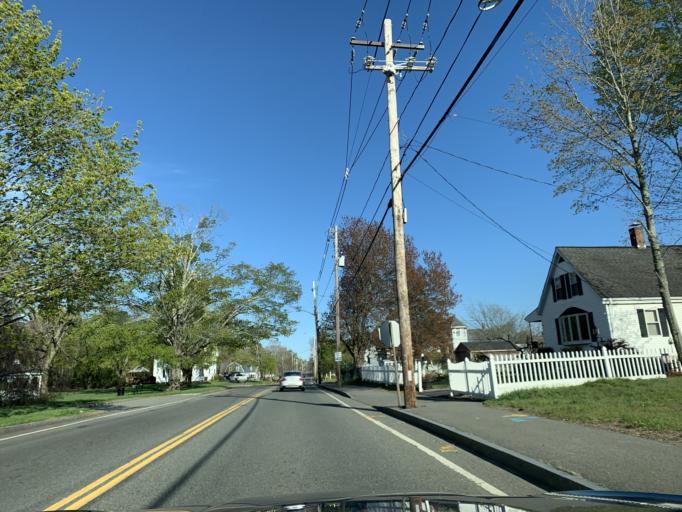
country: US
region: Massachusetts
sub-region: Norfolk County
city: Stoughton
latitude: 42.1307
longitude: -71.1257
